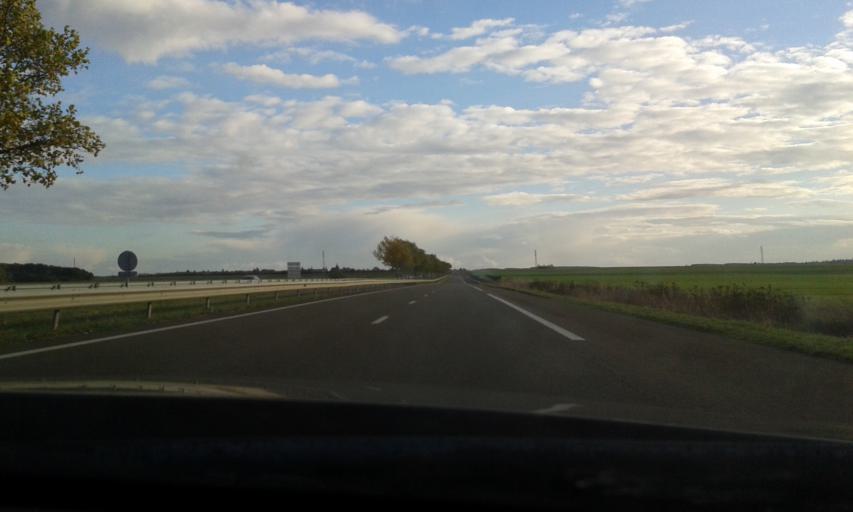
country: FR
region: Centre
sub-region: Departement d'Eure-et-Loir
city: Luray
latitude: 48.6644
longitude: 1.3918
